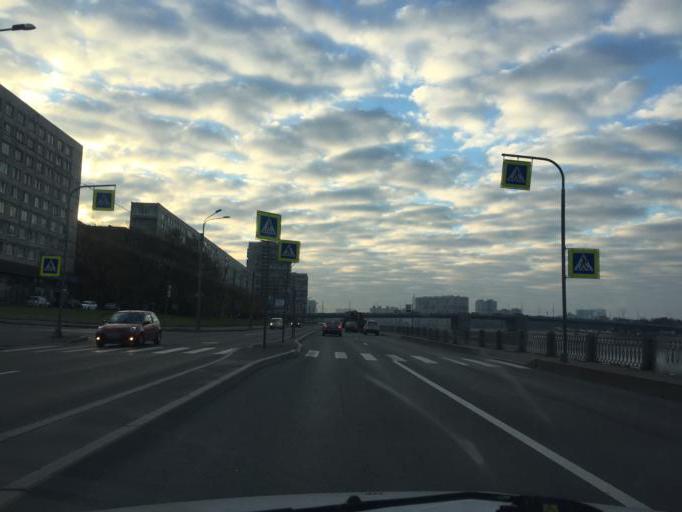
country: RU
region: St.-Petersburg
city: Obukhovo
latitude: 59.8828
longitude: 30.4511
